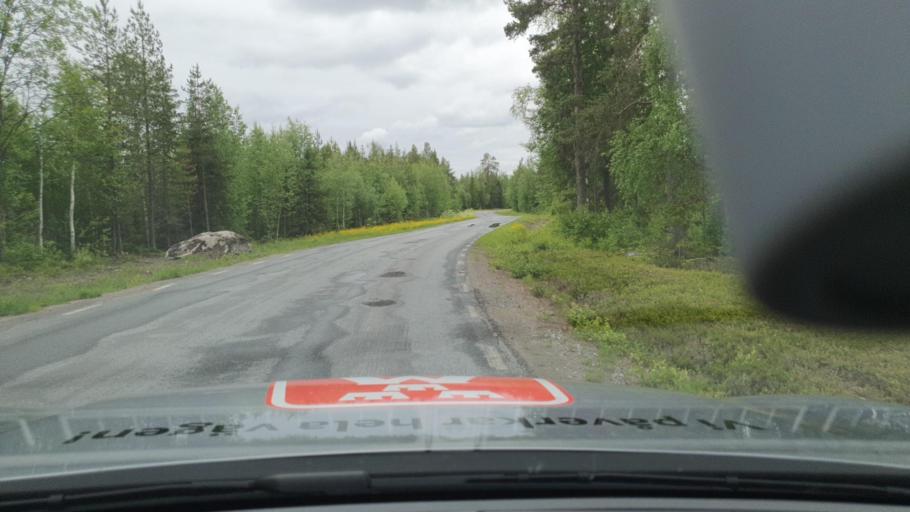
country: SE
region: Norrbotten
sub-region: Lulea Kommun
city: Ranea
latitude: 65.8272
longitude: 22.3211
